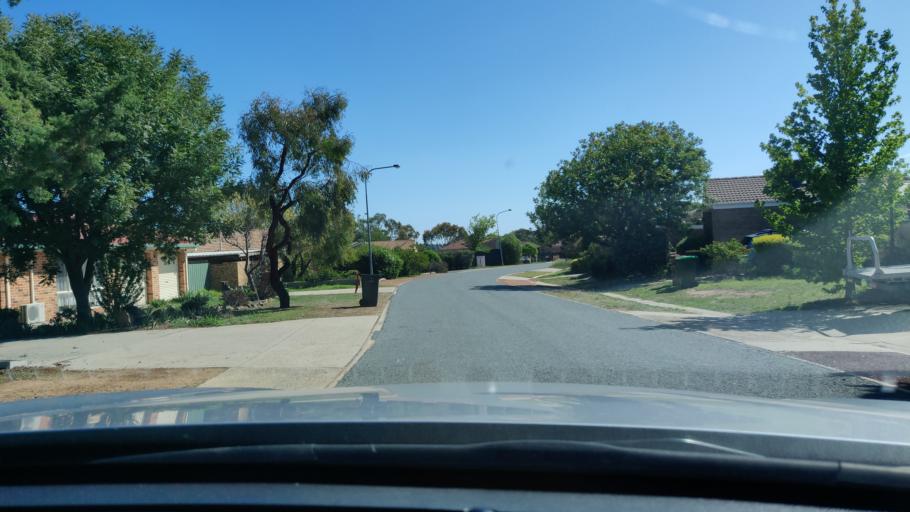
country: AU
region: Australian Capital Territory
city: Macarthur
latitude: -35.4379
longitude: 149.0937
